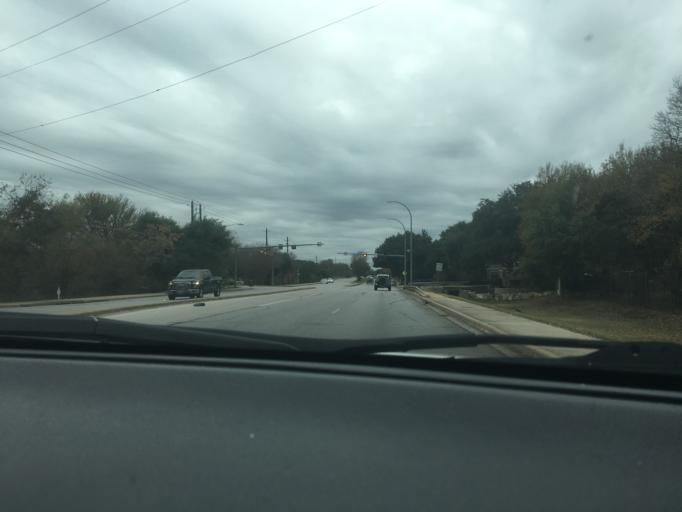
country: US
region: Texas
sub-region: Travis County
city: Rollingwood
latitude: 30.2255
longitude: -97.8231
